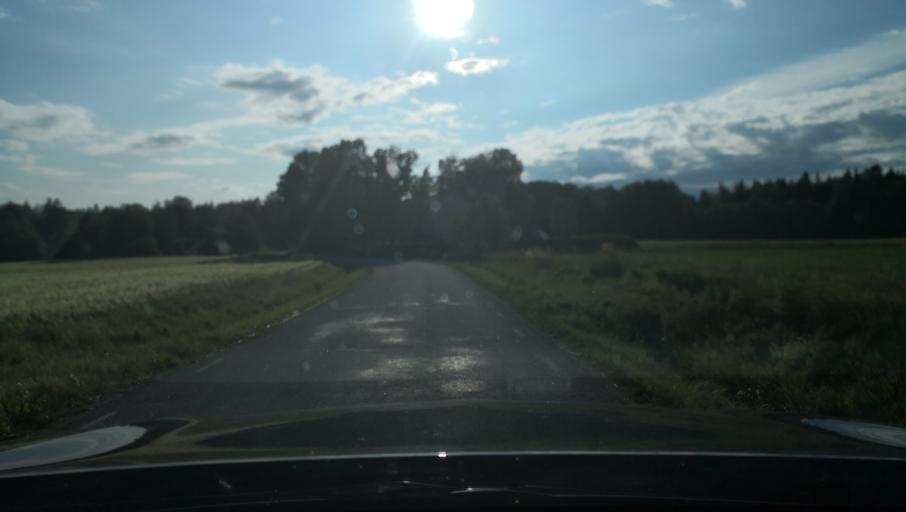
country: SE
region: Uppsala
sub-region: Osthammars Kommun
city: Osterbybruk
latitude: 60.0202
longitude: 17.9639
